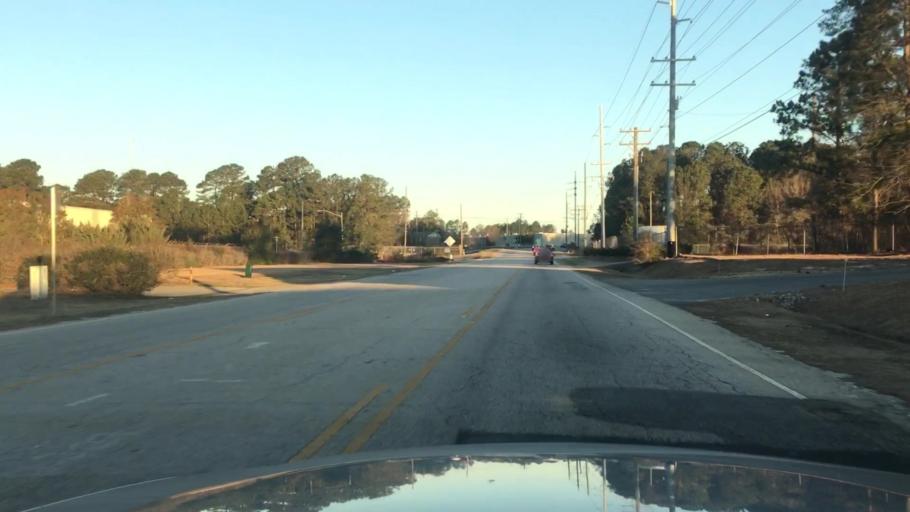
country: US
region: North Carolina
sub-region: Cumberland County
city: Hope Mills
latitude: 34.9980
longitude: -78.9033
